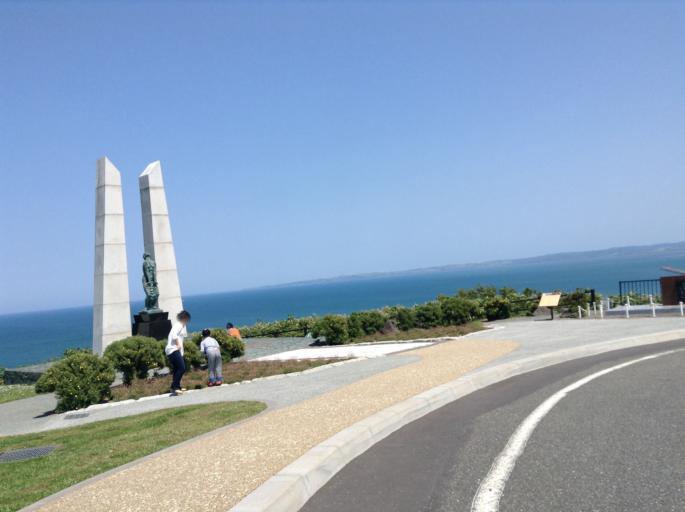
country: JP
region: Hokkaido
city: Wakkanai
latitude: 45.4218
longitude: 141.6680
